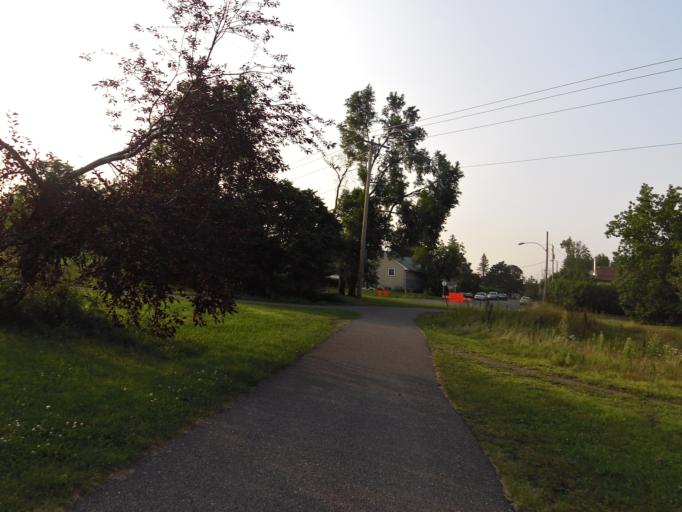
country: CA
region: Ontario
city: Bells Corners
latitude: 45.3906
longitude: -75.8468
